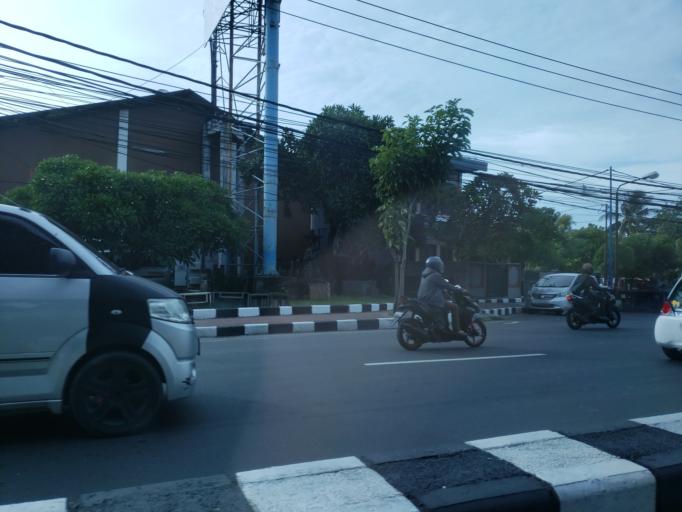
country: ID
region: Bali
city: Jabajero
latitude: -8.7292
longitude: 115.1794
